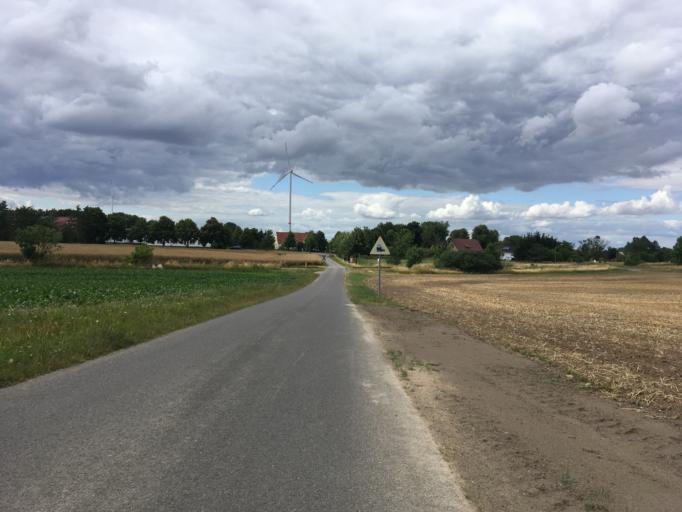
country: DE
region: Brandenburg
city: Gramzow
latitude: 53.2688
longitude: 14.0122
